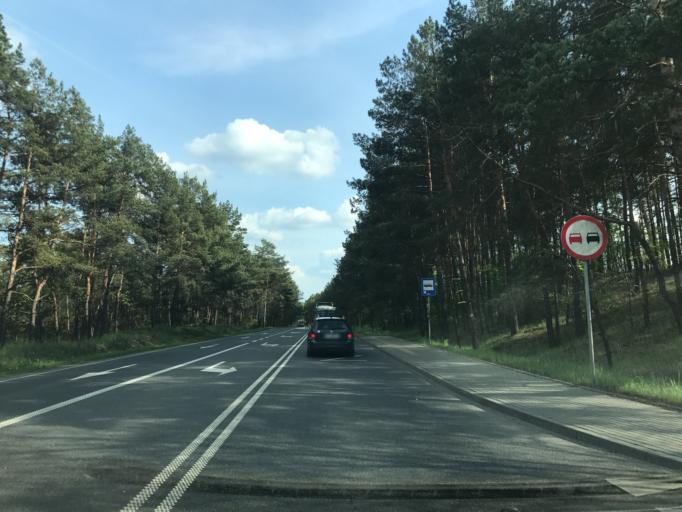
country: PL
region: Kujawsko-Pomorskie
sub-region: Bydgoszcz
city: Fordon
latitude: 53.0842
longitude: 18.1189
